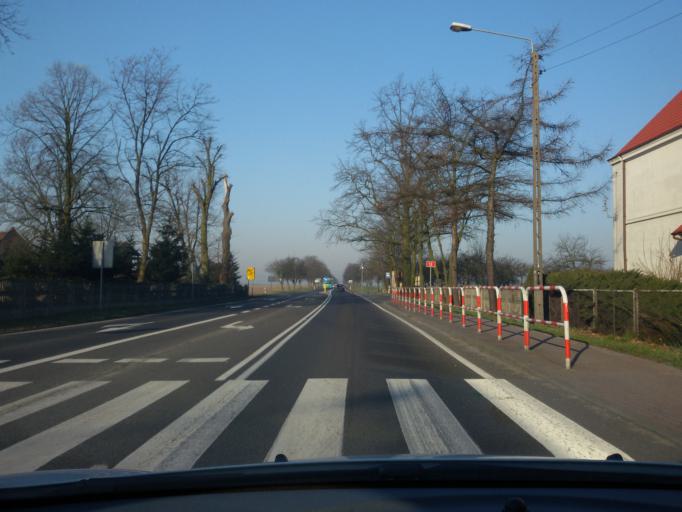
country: PL
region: Greater Poland Voivodeship
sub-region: Powiat leszczynski
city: Swieciechowa
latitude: 51.8247
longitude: 16.4426
